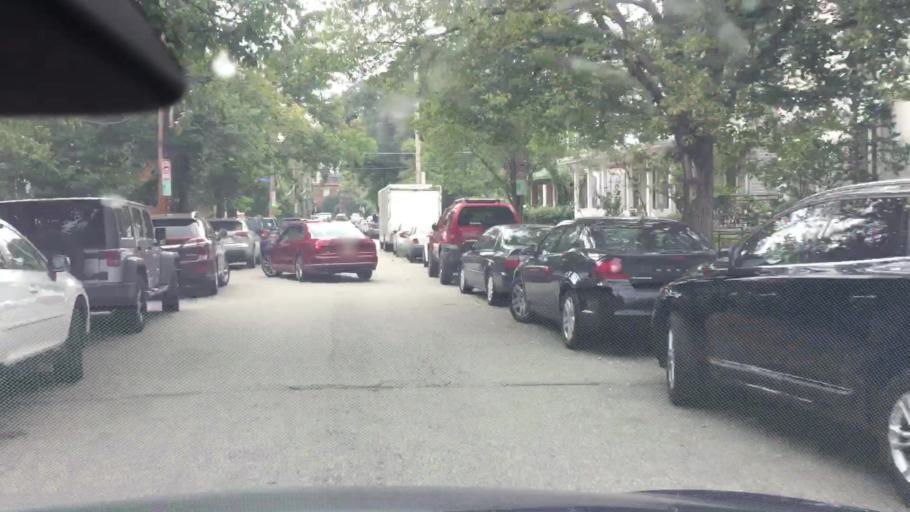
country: US
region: Pennsylvania
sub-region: Allegheny County
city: Bloomfield
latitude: 40.4506
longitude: -79.9324
